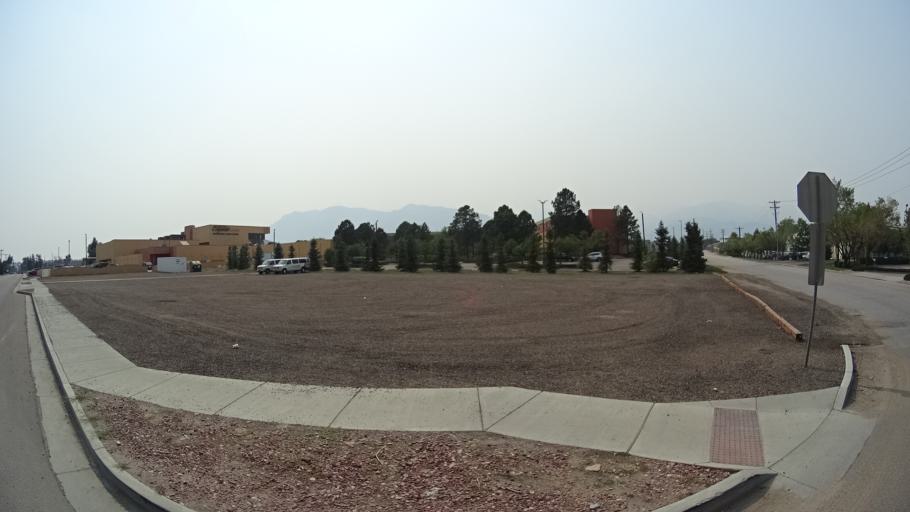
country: US
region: Colorado
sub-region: El Paso County
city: Stratmoor
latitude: 38.7997
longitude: -104.7944
